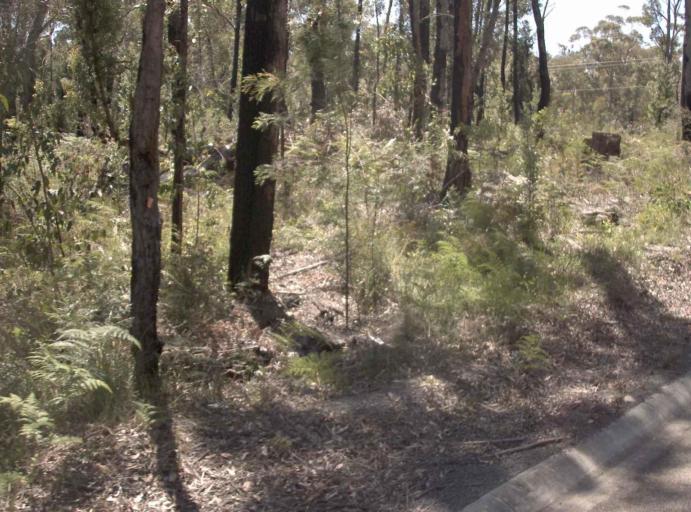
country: AU
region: Victoria
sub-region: East Gippsland
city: Lakes Entrance
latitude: -37.6924
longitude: 148.7494
